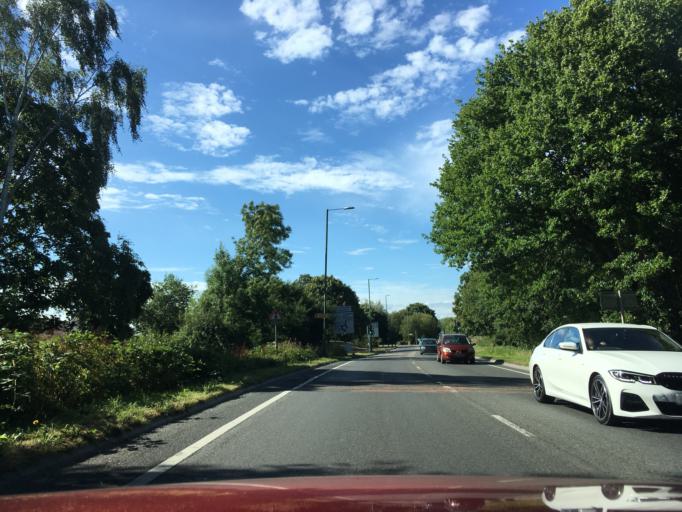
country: GB
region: England
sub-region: Dorset
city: Ferndown
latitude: 50.7662
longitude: -1.8834
